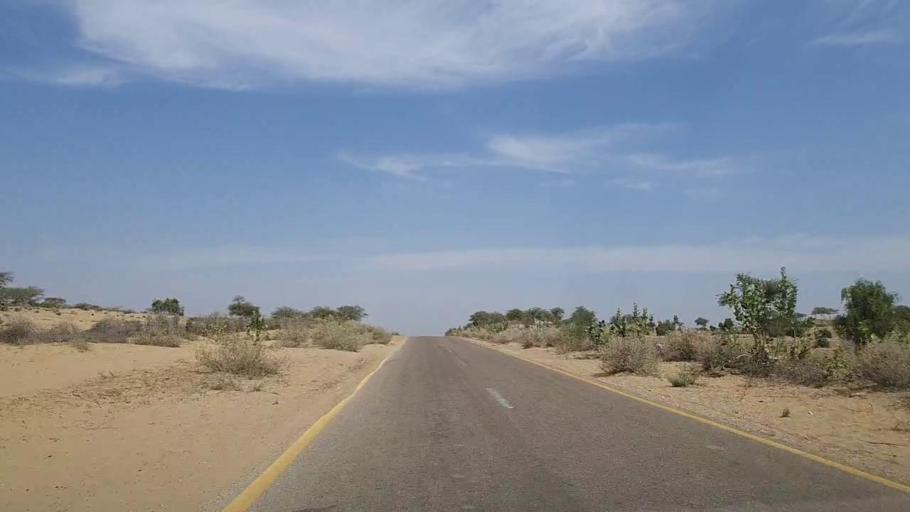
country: PK
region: Sindh
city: Mithi
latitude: 24.8113
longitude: 69.8172
